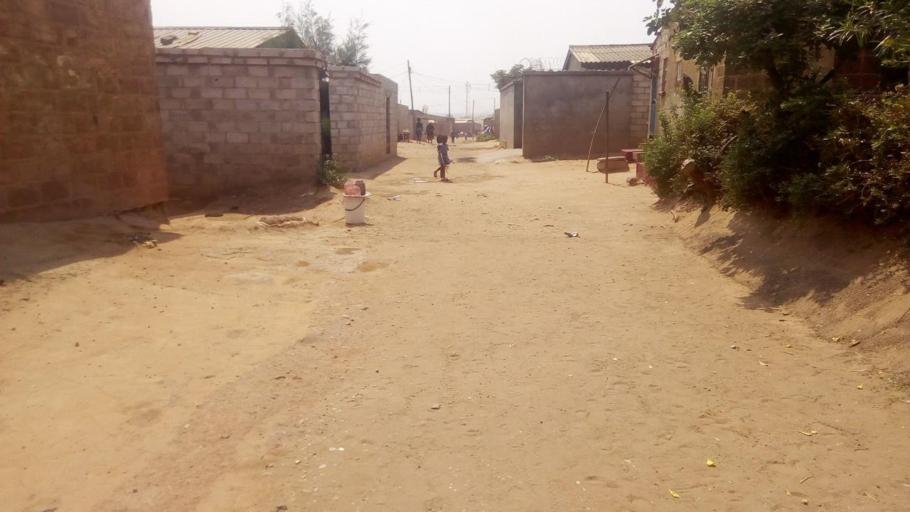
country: ZM
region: Lusaka
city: Lusaka
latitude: -15.3584
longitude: 28.2935
